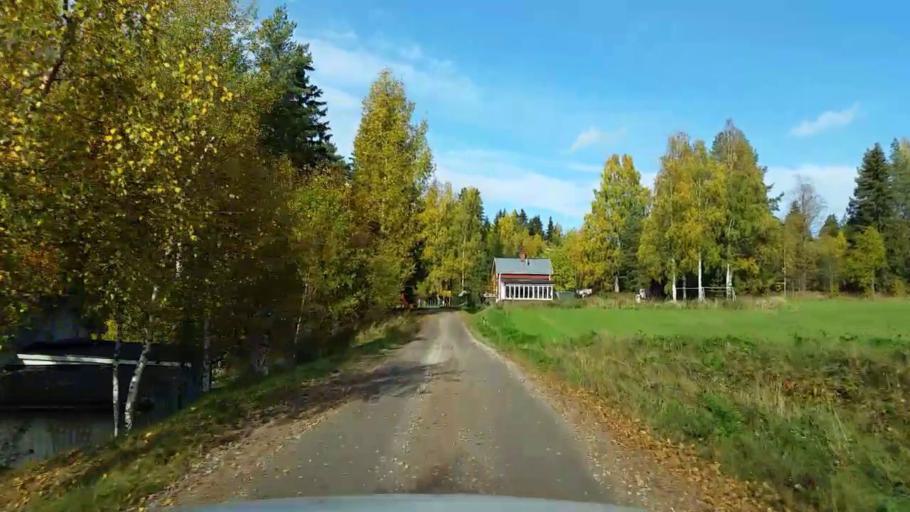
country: SE
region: Gaevleborg
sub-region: Ljusdals Kommun
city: Jaervsoe
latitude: 61.7859
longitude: 16.1531
